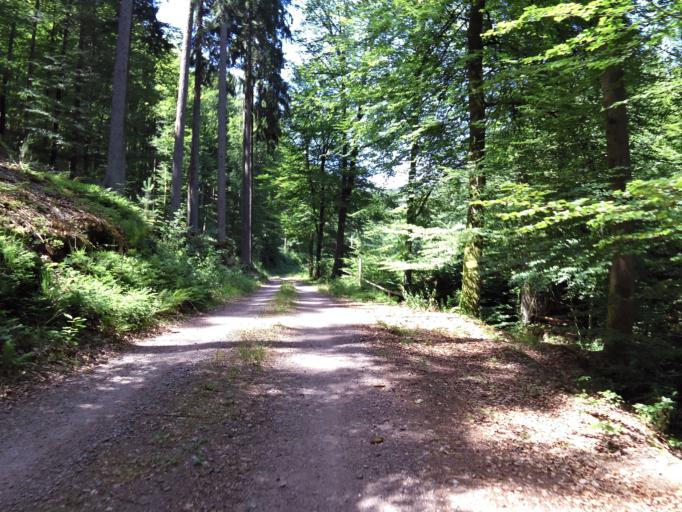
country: DE
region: Rheinland-Pfalz
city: Wilgartswiesen
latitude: 49.2674
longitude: 7.8678
